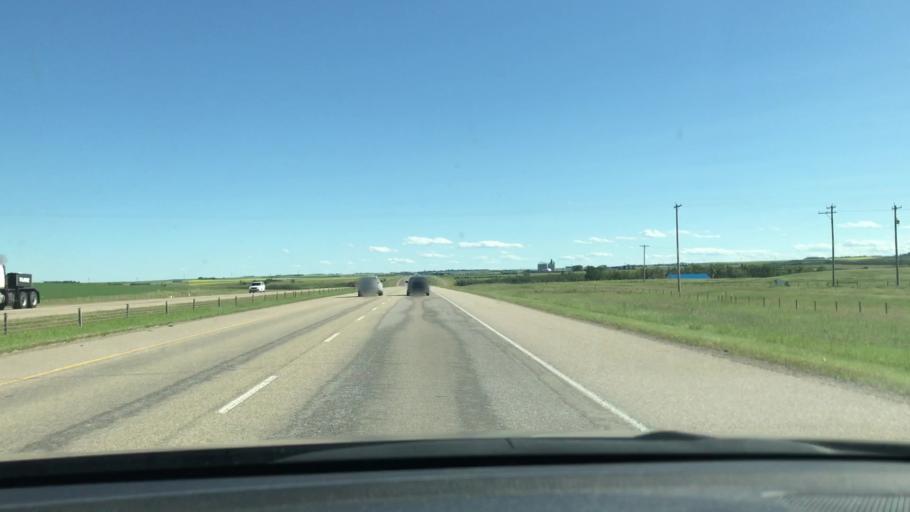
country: CA
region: Alberta
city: Carstairs
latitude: 51.5267
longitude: -114.0253
